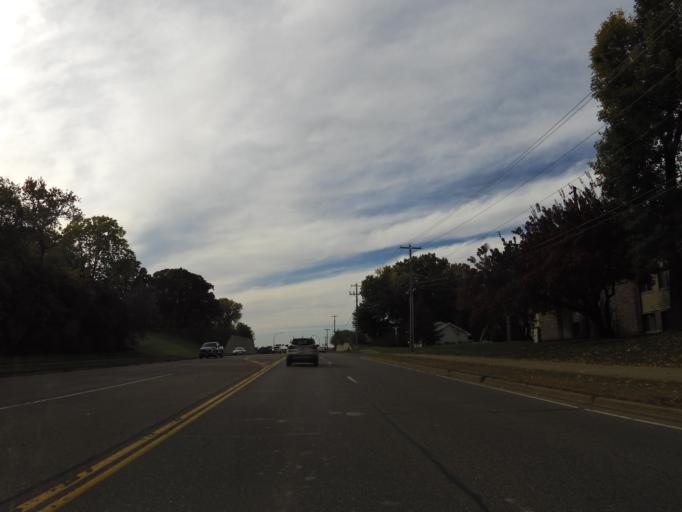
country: US
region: Minnesota
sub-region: Dakota County
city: Eagan
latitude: 44.8337
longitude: -93.1839
